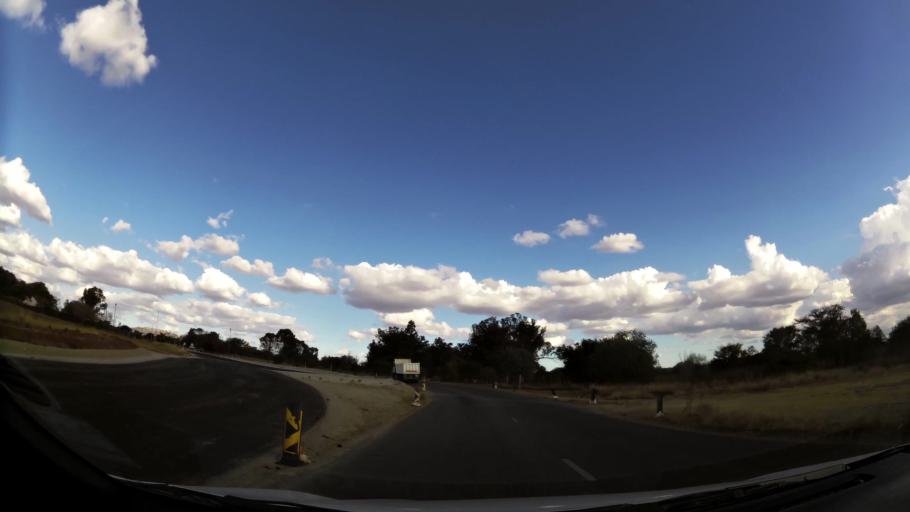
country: ZA
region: Limpopo
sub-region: Capricorn District Municipality
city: Polokwane
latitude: -23.9336
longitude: 29.4719
